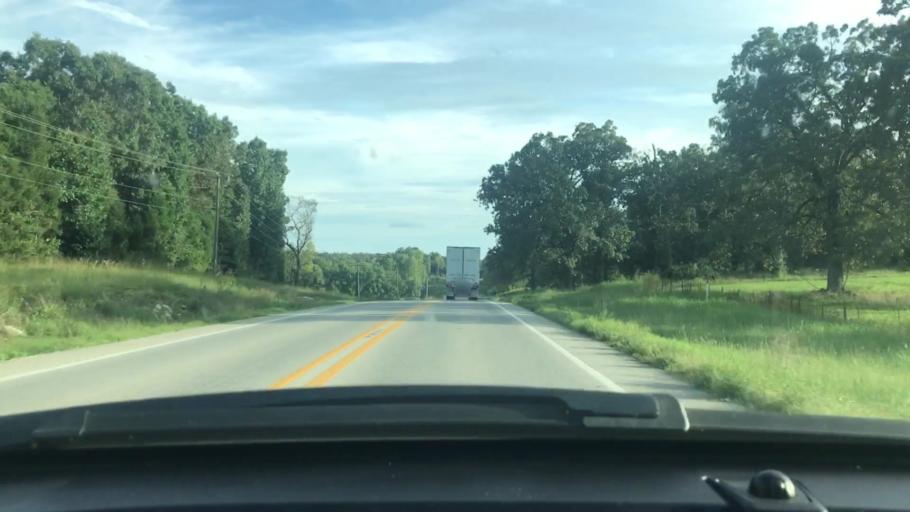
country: US
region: Arkansas
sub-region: Randolph County
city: Pocahontas
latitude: 36.1611
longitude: -91.1622
